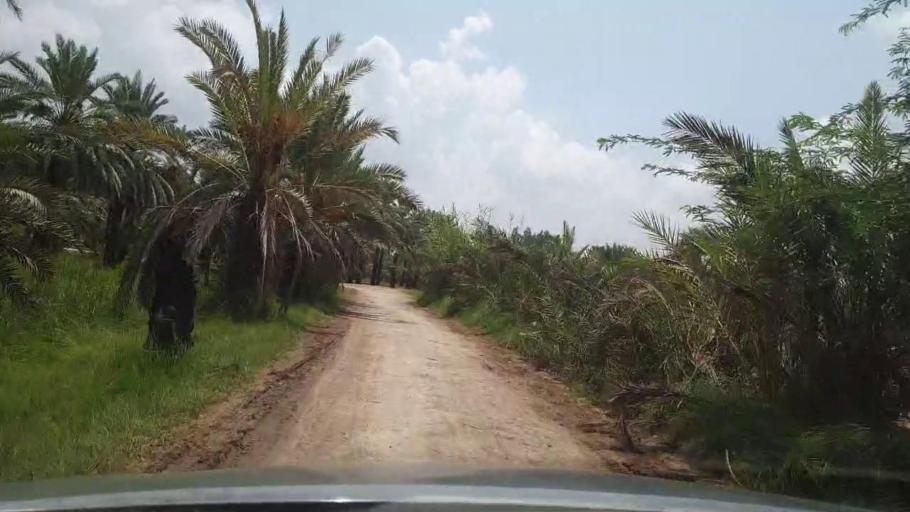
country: PK
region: Sindh
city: Khairpur
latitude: 27.6311
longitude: 68.7348
